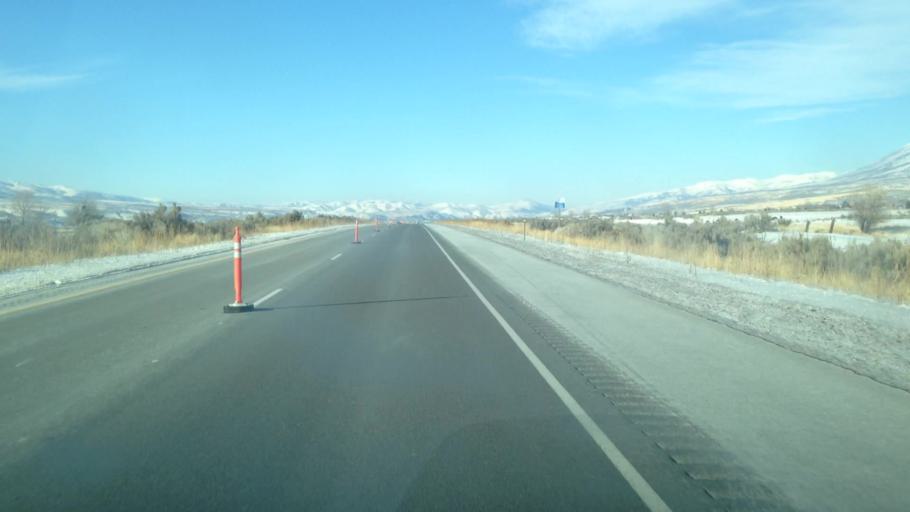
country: US
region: Idaho
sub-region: Bannock County
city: Pocatello
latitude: 42.6304
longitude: -112.2029
